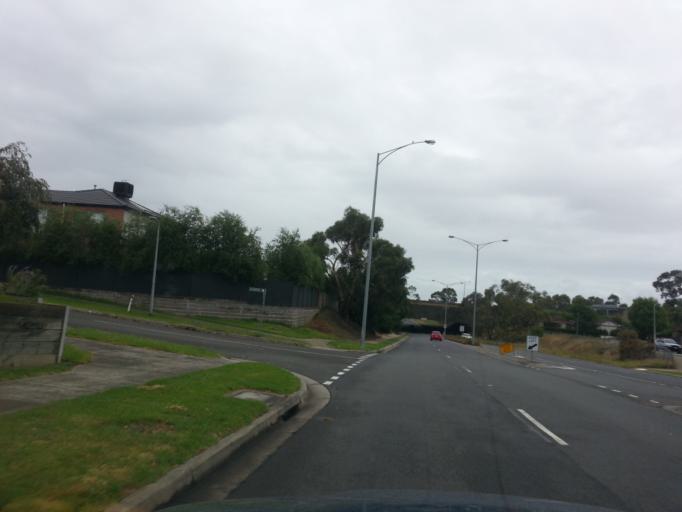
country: AU
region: Victoria
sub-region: Casey
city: Narre Warren
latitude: -38.0139
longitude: 145.3073
